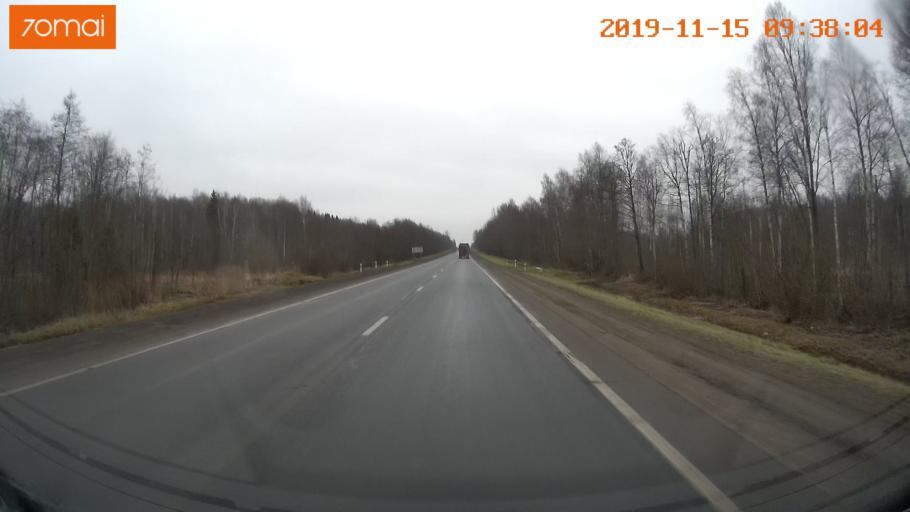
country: RU
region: Vologda
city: Sheksna
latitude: 59.2353
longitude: 38.4484
